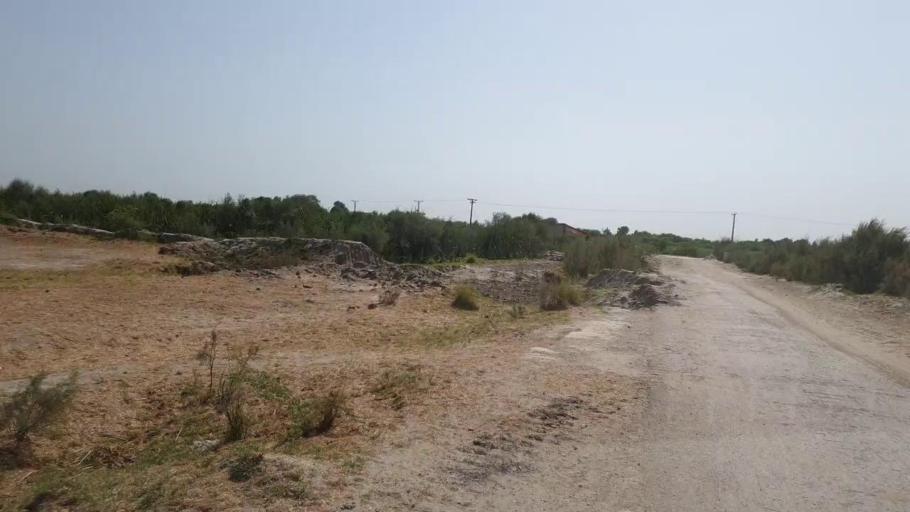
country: PK
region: Sindh
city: Jam Sahib
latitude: 26.4121
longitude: 68.9111
